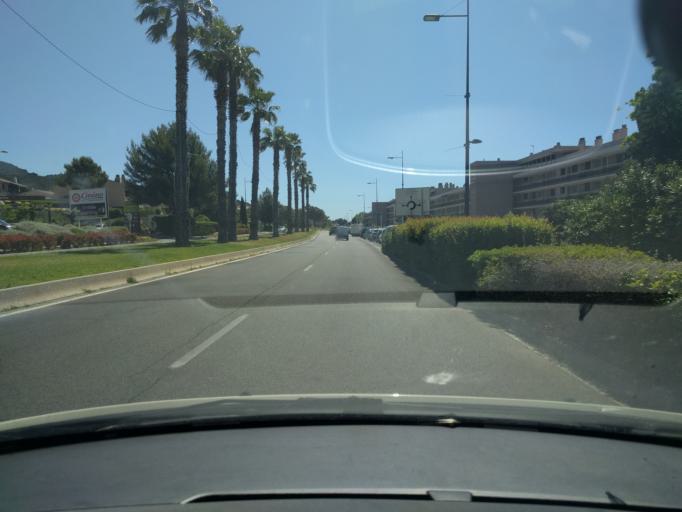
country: FR
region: Provence-Alpes-Cote d'Azur
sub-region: Departement du Var
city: Carqueiranne
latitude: 43.0920
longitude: 6.0781
